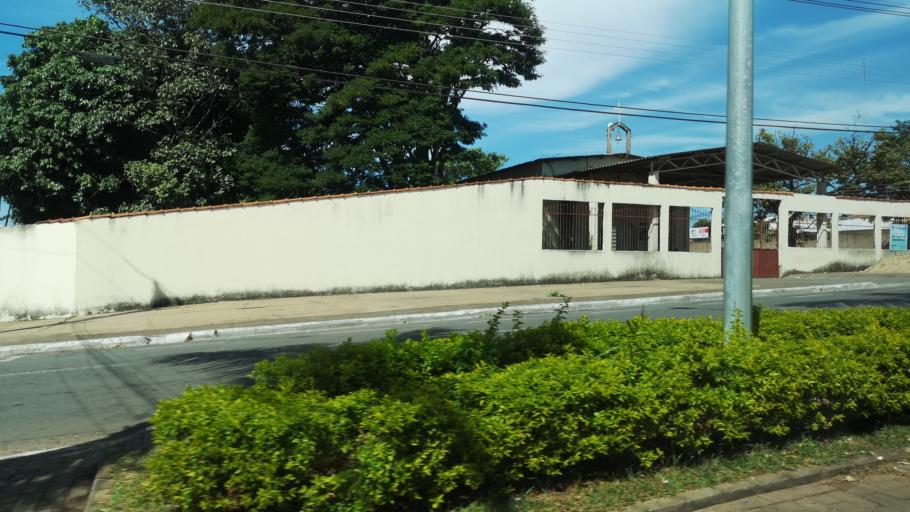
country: BR
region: Goias
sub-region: Senador Canedo
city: Senador Canedo
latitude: -16.6940
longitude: -49.0997
